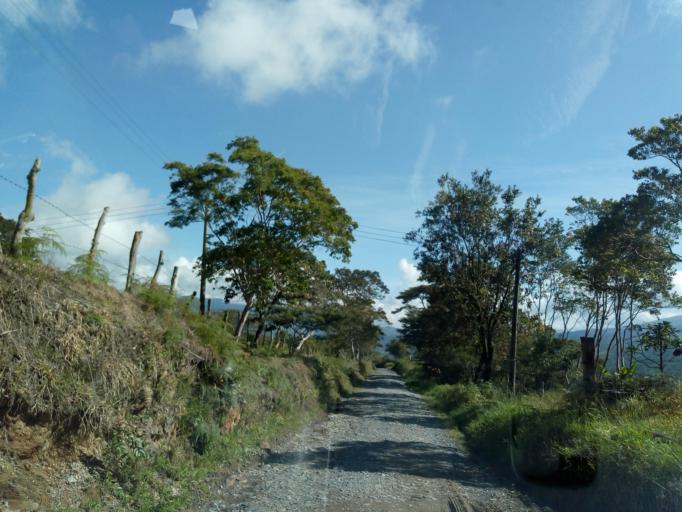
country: CO
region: Boyaca
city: Moniquira
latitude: 5.8870
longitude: -73.5371
